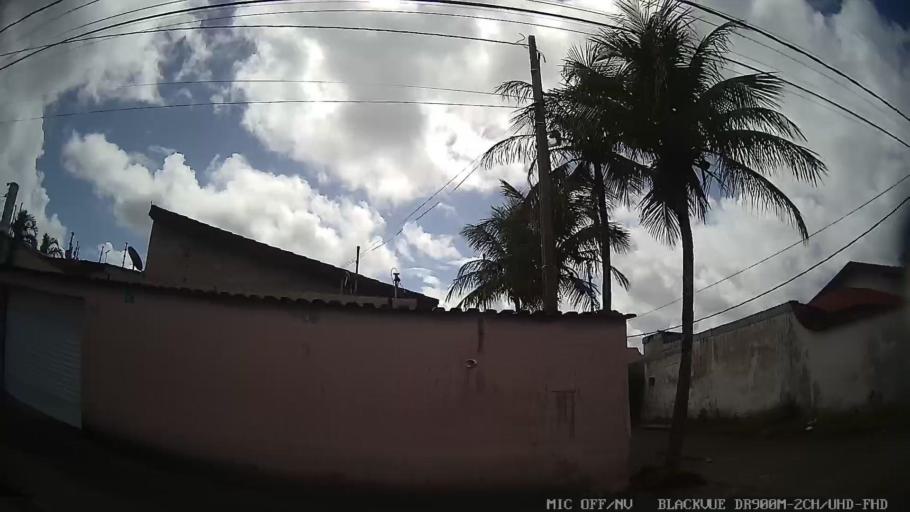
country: BR
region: Sao Paulo
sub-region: Itanhaem
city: Itanhaem
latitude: -24.2014
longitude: -46.8201
